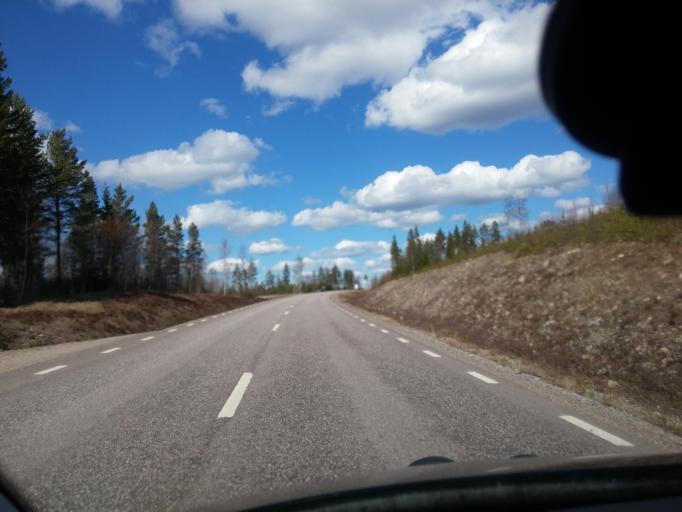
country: SE
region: Gaevleborg
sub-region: Ovanakers Kommun
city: Edsbyn
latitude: 61.2370
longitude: 15.8812
